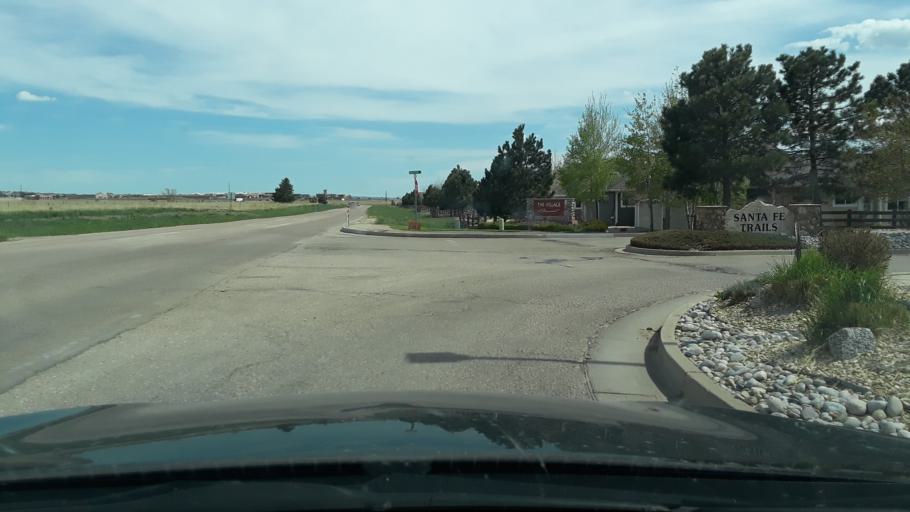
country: US
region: Colorado
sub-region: El Paso County
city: Monument
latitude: 39.0770
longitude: -104.8634
